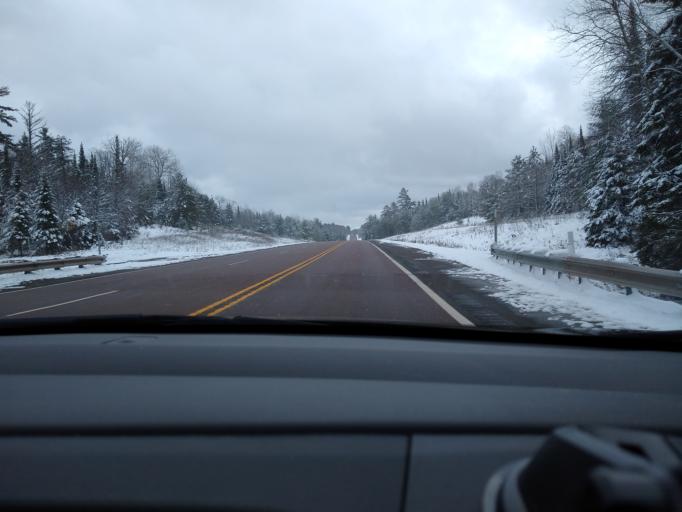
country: US
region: Wisconsin
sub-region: Vilas County
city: Eagle River
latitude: 46.1964
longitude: -89.0041
